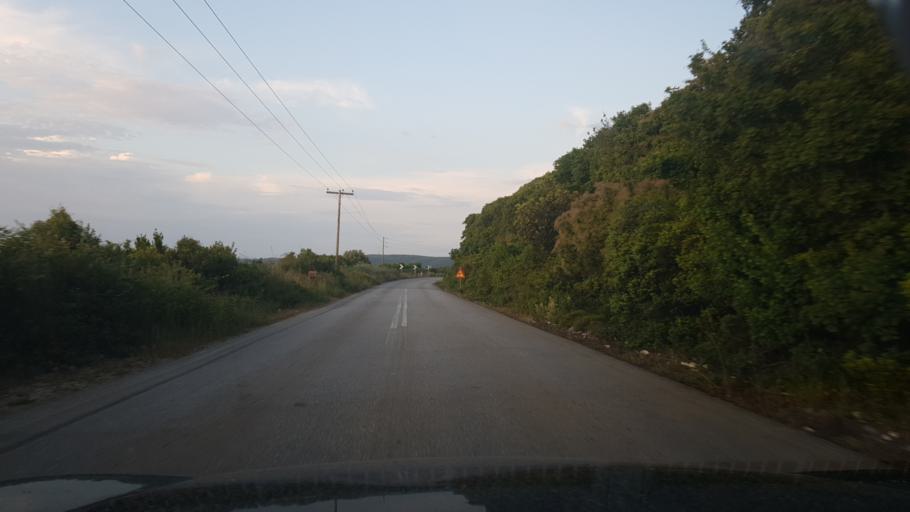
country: GR
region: Ionian Islands
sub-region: Lefkada
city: Lefkada
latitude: 38.8594
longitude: 20.7544
